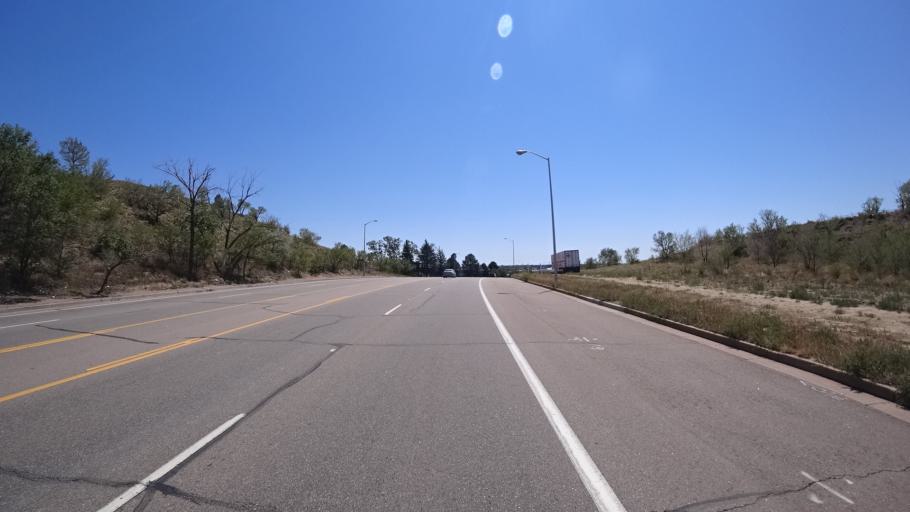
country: US
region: Colorado
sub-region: El Paso County
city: Stratmoor
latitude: 38.7962
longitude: -104.7717
